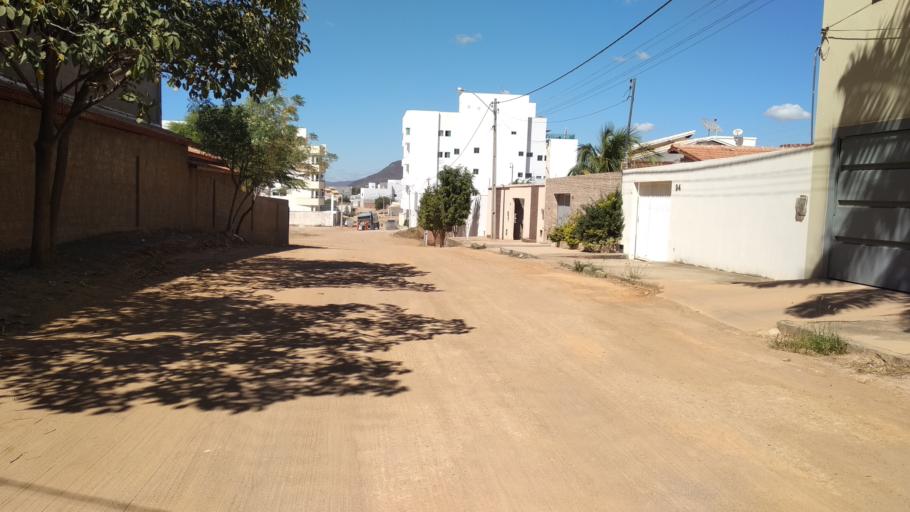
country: BR
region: Bahia
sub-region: Guanambi
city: Guanambi
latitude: -14.2303
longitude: -42.7765
